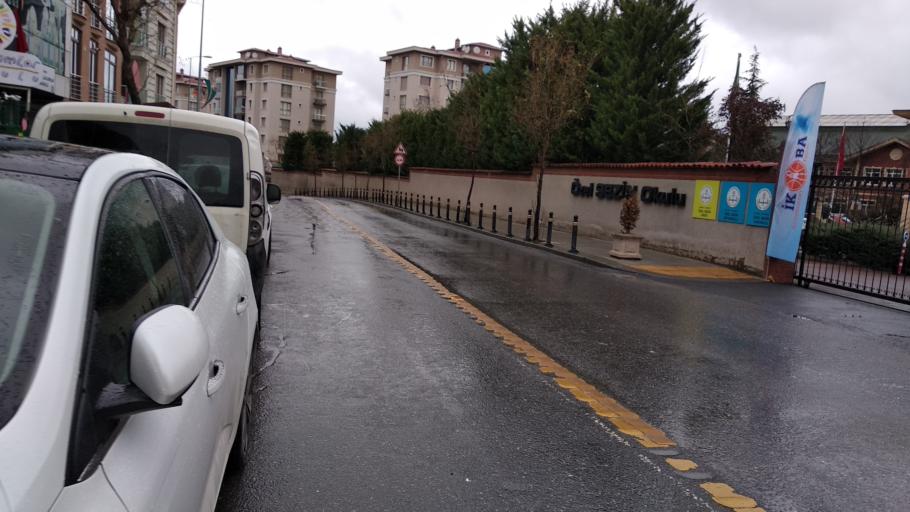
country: TR
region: Istanbul
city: Samandira
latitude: 41.0237
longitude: 29.1842
